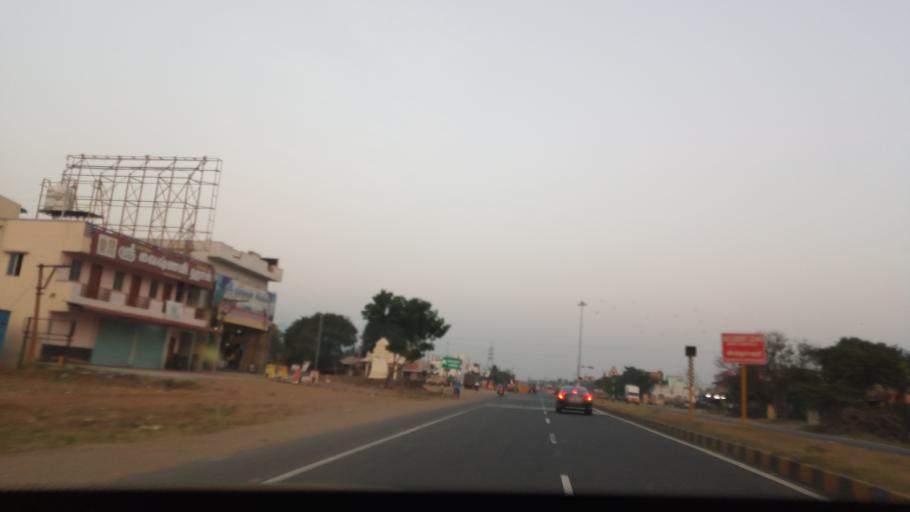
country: IN
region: Tamil Nadu
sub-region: Salem
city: Salem
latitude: 11.6658
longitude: 78.2693
